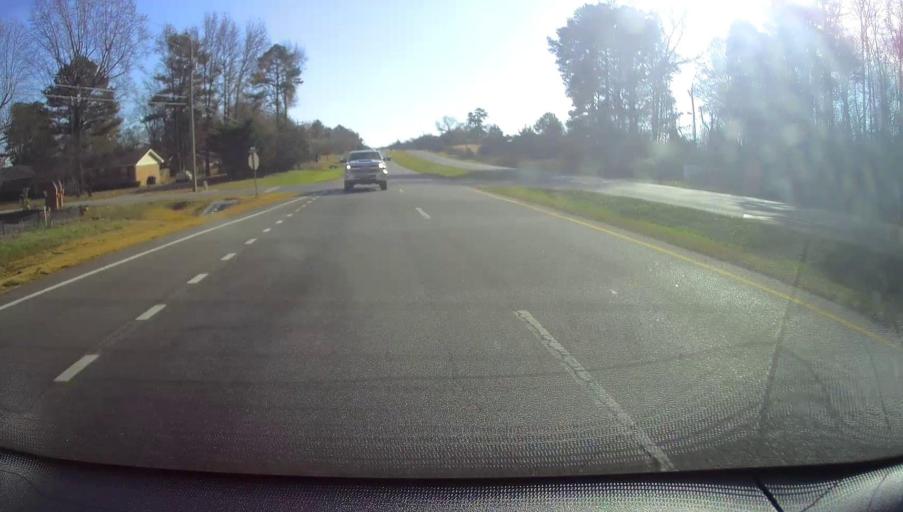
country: US
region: Alabama
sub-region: Limestone County
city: Athens
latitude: 34.7559
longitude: -86.9570
